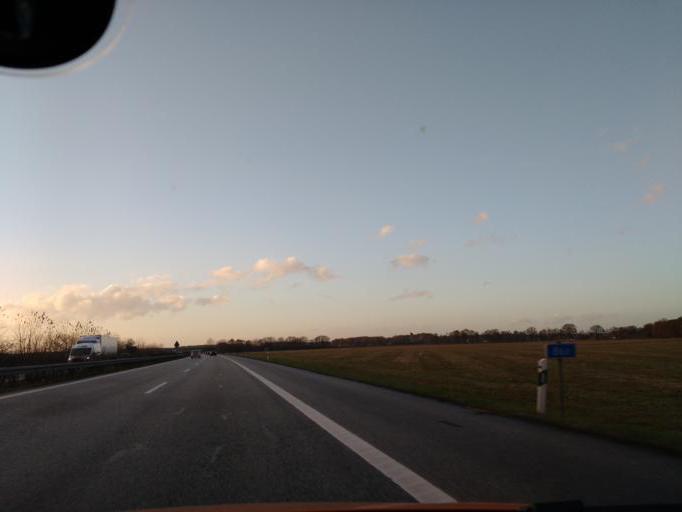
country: DE
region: Mecklenburg-Vorpommern
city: Sulstorf
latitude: 53.4686
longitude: 11.3275
